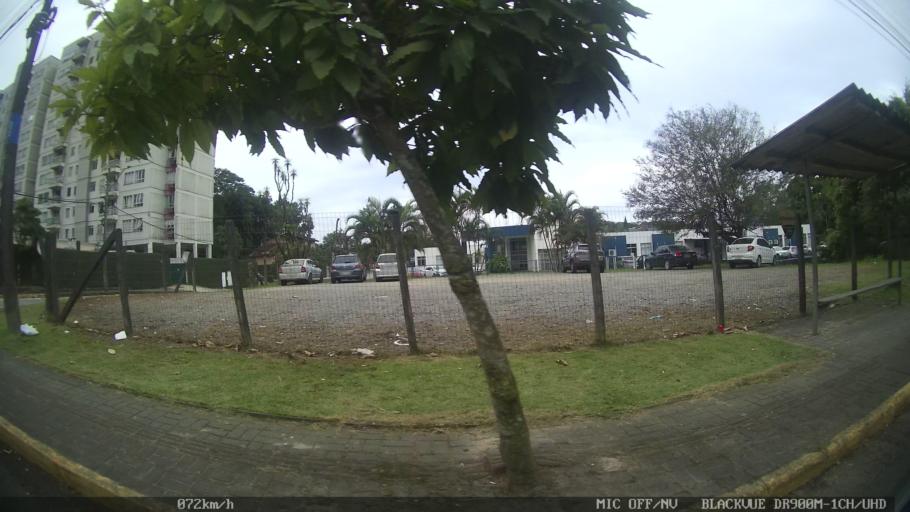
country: BR
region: Santa Catarina
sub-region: Joinville
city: Joinville
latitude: -26.3096
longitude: -48.8630
